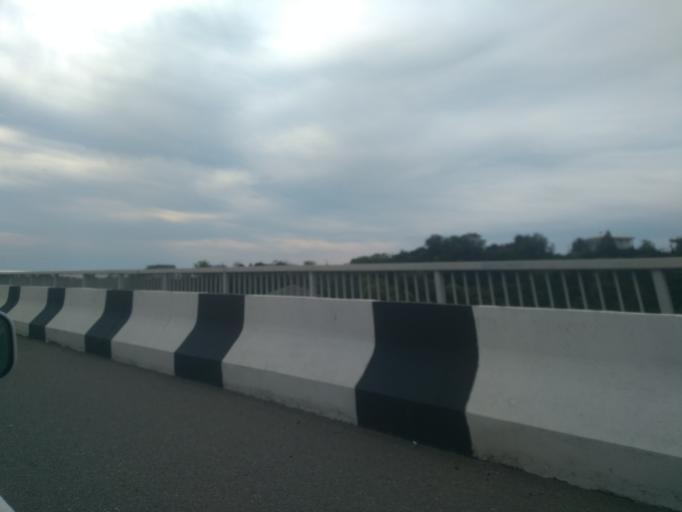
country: GE
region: Ajaria
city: Kobuleti
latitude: 41.7360
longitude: 41.7562
